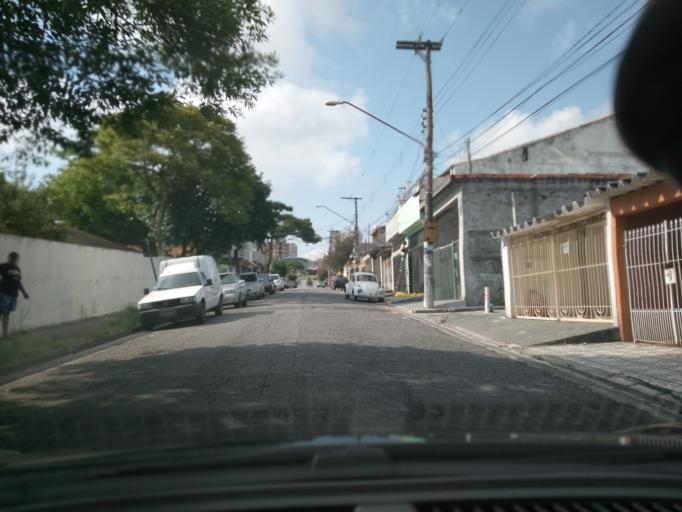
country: BR
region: Sao Paulo
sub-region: Sao Bernardo Do Campo
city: Sao Bernardo do Campo
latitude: -23.7302
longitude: -46.5761
